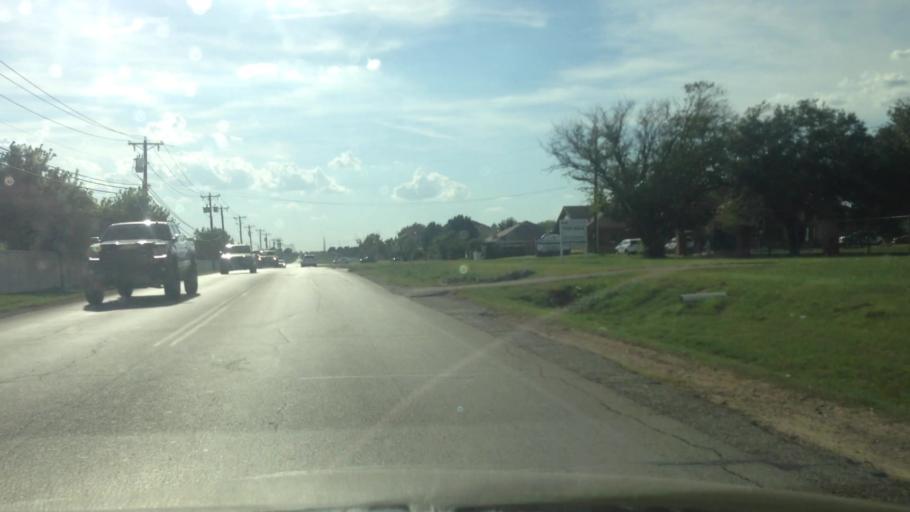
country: US
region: Texas
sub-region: Tarrant County
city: Haslet
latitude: 32.9244
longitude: -97.3695
